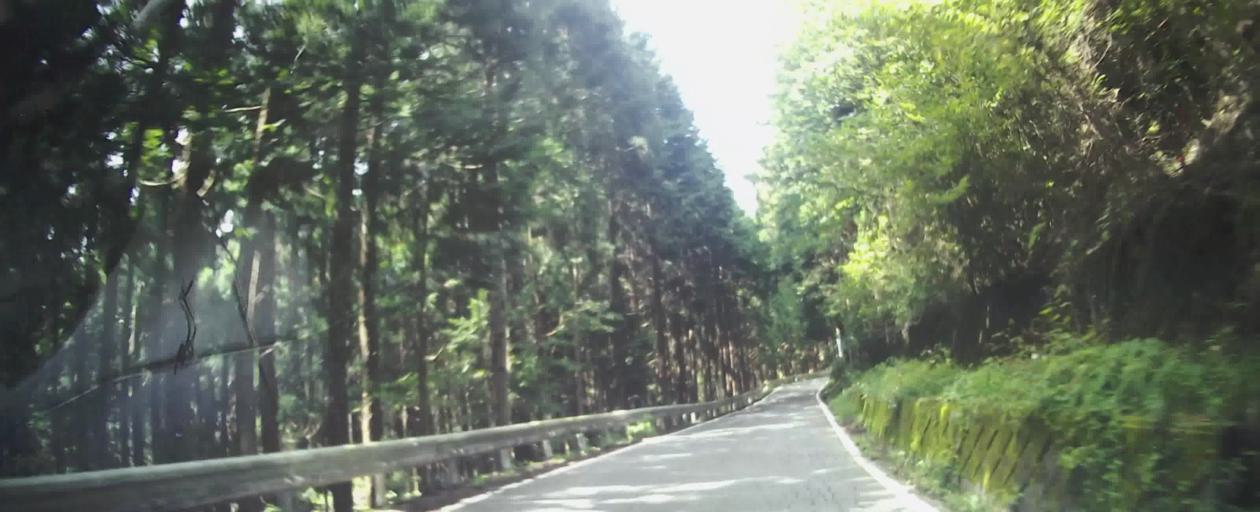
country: JP
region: Gunma
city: Shibukawa
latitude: 36.4528
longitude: 138.9002
